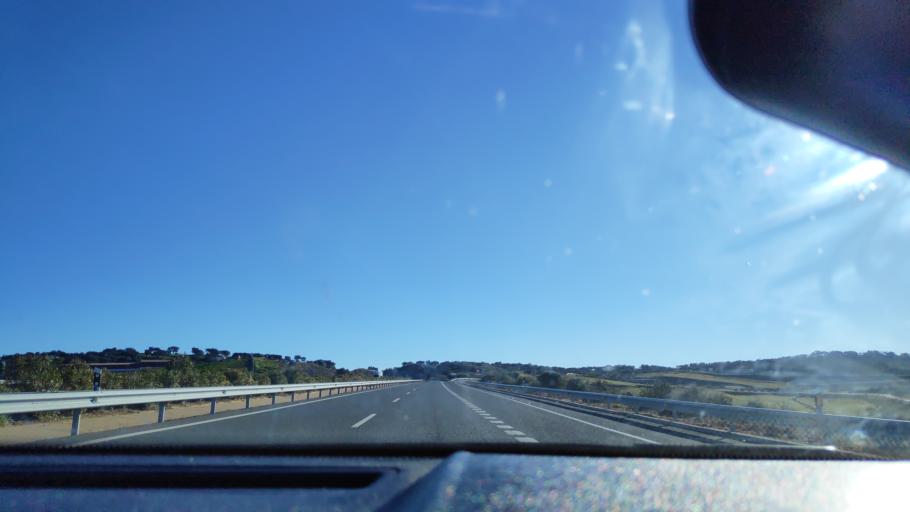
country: ES
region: Extremadura
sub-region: Provincia de Badajoz
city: Monesterio
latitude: 38.1399
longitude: -6.2749
